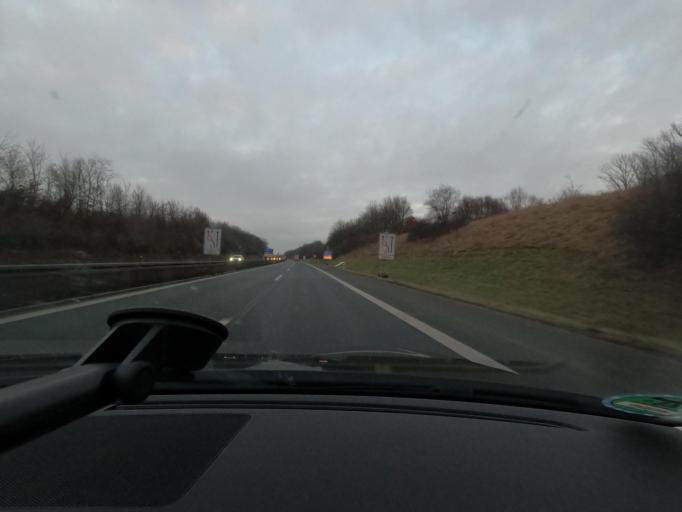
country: DE
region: Bavaria
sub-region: Upper Franconia
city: Hirschaid
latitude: 49.8339
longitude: 11.0059
